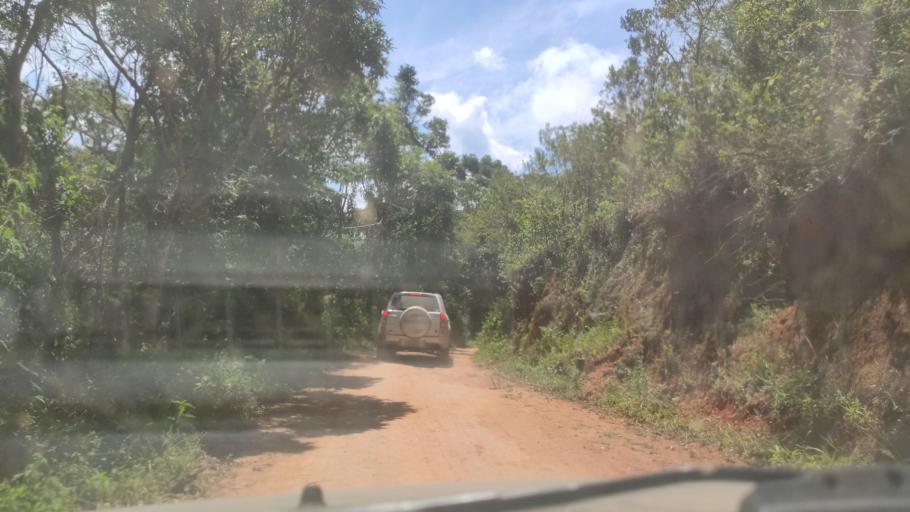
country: BR
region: Minas Gerais
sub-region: Cambui
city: Cambui
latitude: -22.6827
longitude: -45.9764
